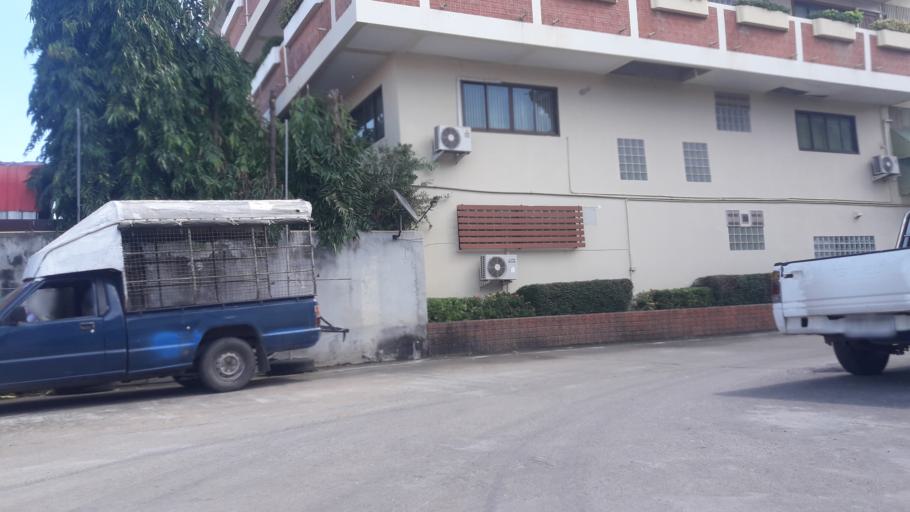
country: TH
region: Phichit
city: Thap Khlo
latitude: 16.1678
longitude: 100.5804
